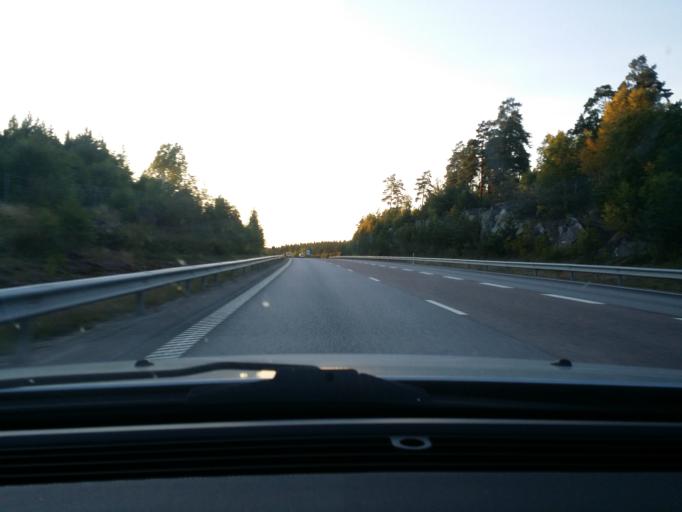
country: SE
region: Uppsala
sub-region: Enkopings Kommun
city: Dalby
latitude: 59.6182
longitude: 17.4020
